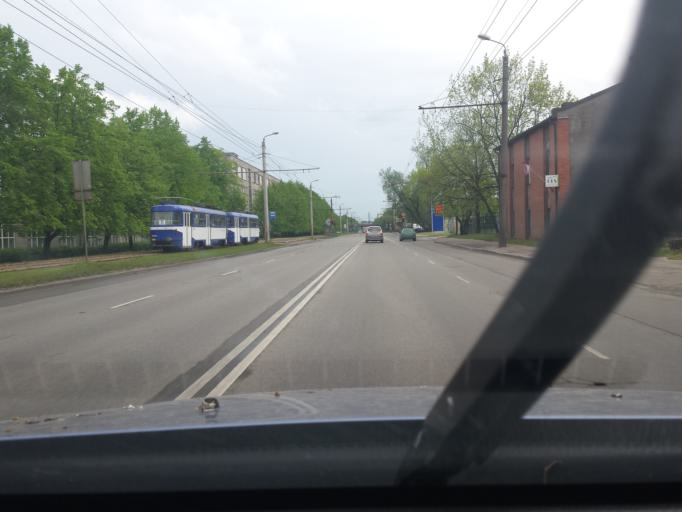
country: LV
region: Riga
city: Riga
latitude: 56.9807
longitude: 24.1167
